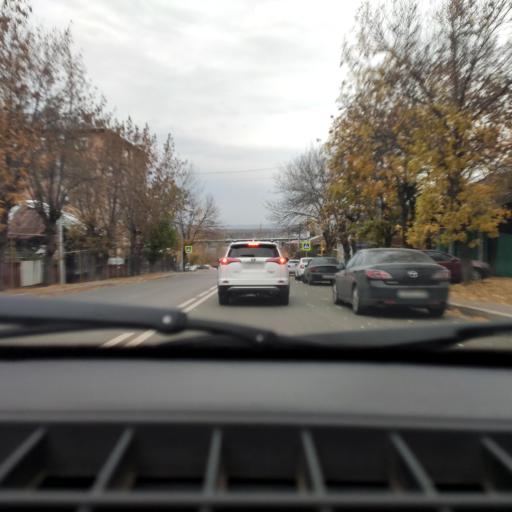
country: RU
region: Bashkortostan
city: Ufa
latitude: 54.7491
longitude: 55.9609
